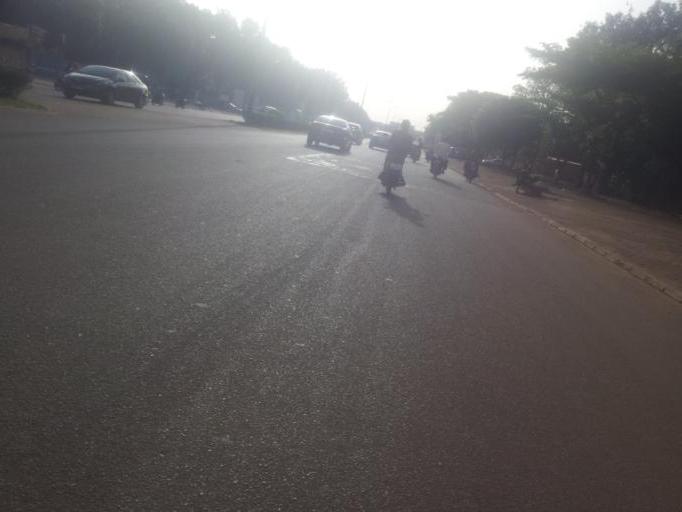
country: BF
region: Centre
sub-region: Kadiogo Province
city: Ouagadougou
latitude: 12.3726
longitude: -1.5137
